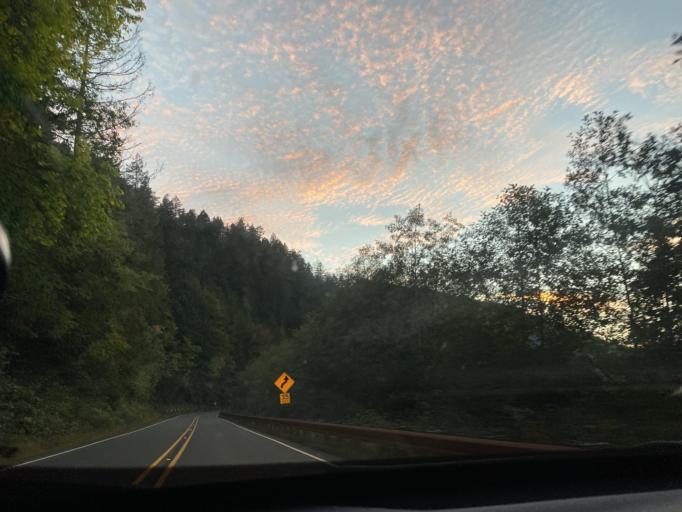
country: CA
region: British Columbia
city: Sooke
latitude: 48.0768
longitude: -123.7614
